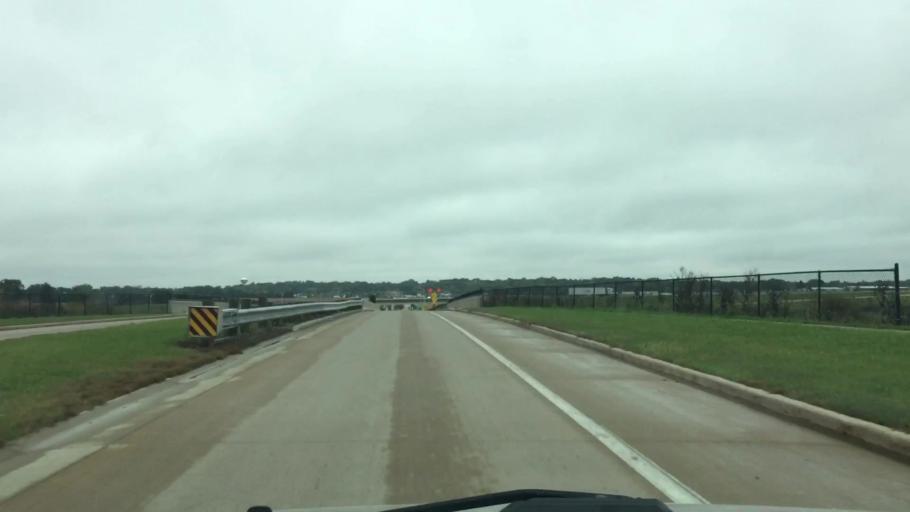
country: US
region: Wisconsin
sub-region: Rock County
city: Milton
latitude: 42.7690
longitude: -88.9189
